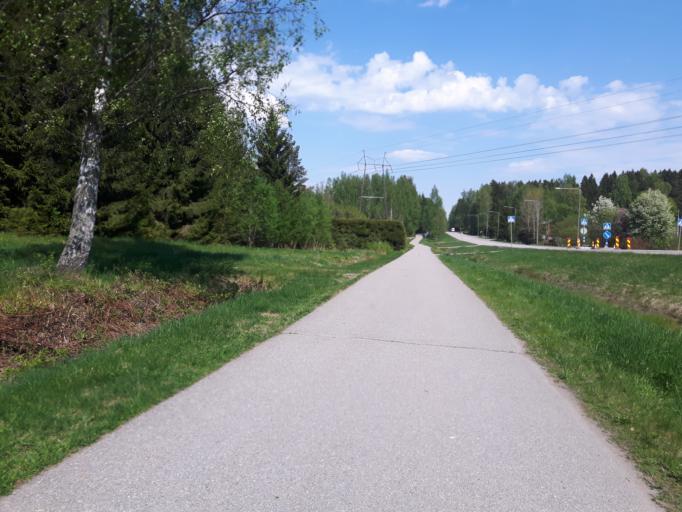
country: FI
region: Uusimaa
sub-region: Porvoo
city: Porvoo
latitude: 60.3841
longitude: 25.6241
